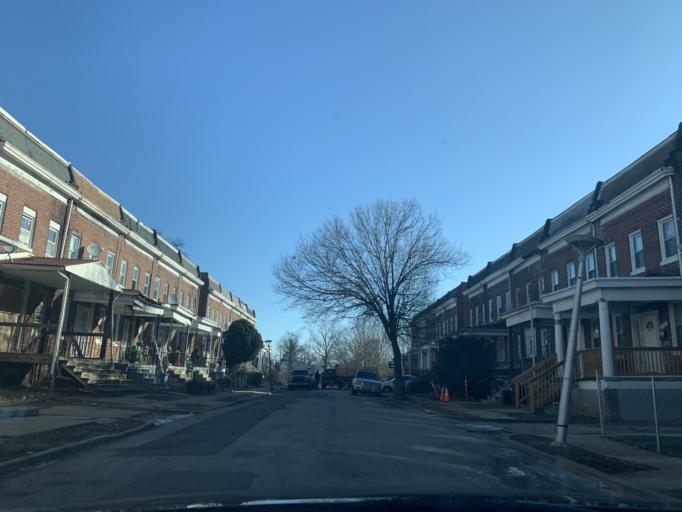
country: US
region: Maryland
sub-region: Baltimore County
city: Lochearn
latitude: 39.3367
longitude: -76.6837
